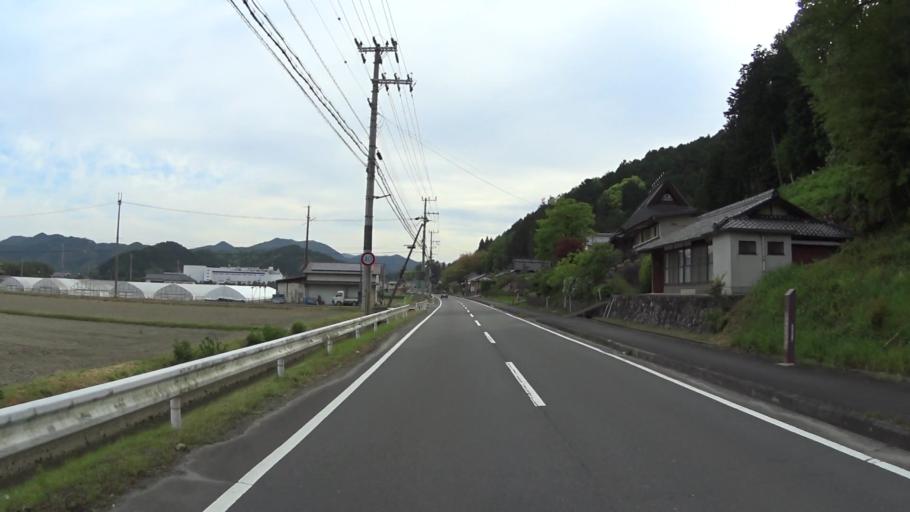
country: JP
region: Kyoto
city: Kameoka
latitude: 35.1008
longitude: 135.5113
